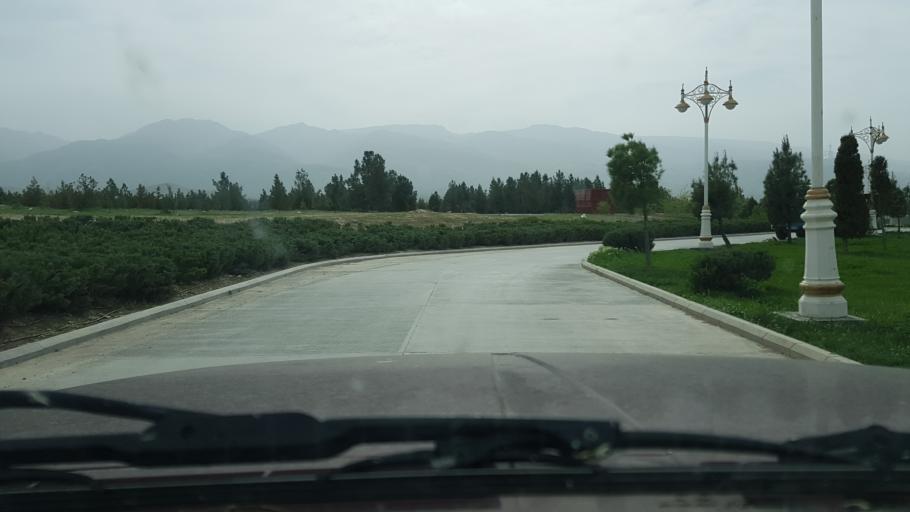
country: TM
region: Ahal
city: Ashgabat
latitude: 37.8812
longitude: 58.3357
